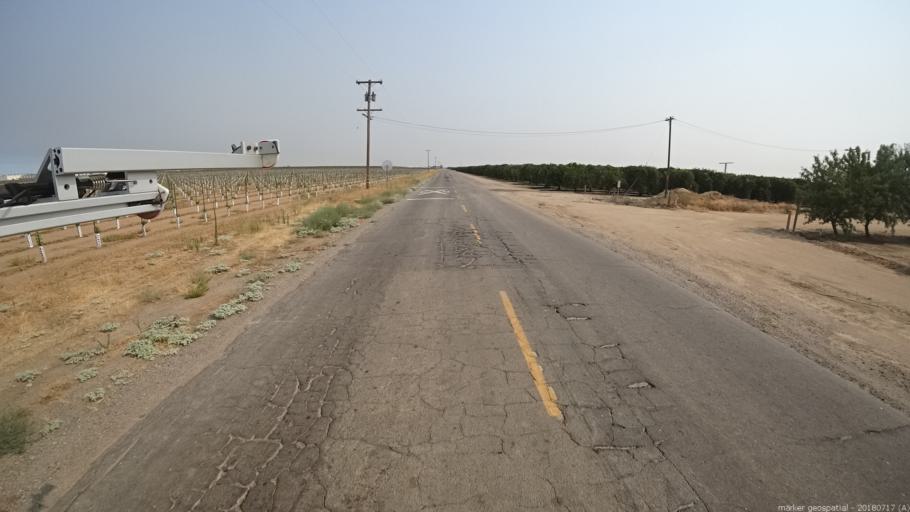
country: US
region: California
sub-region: Madera County
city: Madera Acres
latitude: 37.0723
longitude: -120.1109
